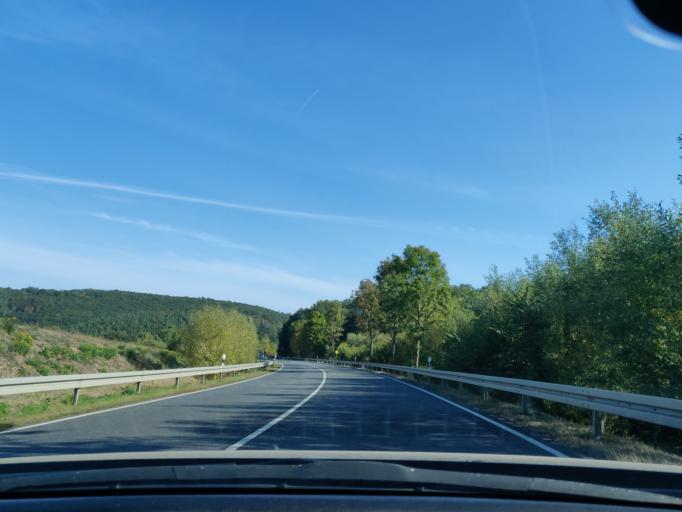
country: DE
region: Hesse
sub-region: Regierungsbezirk Kassel
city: Bad Wildungen
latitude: 51.1202
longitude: 9.1557
